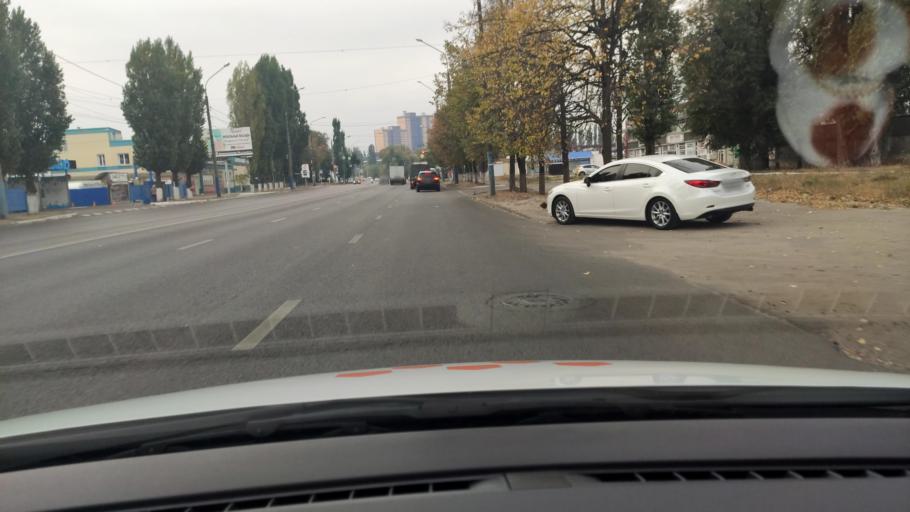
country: RU
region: Voronezj
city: Voronezh
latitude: 51.6831
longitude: 39.1658
